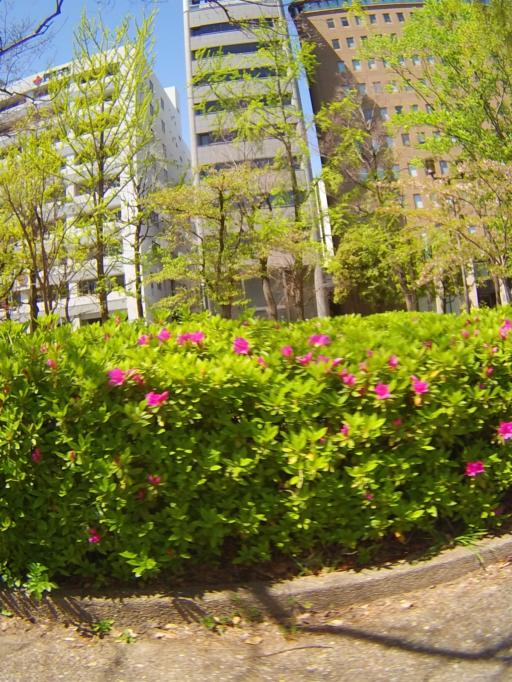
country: JP
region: Osaka
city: Osaka-shi
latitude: 34.6879
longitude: 135.5205
